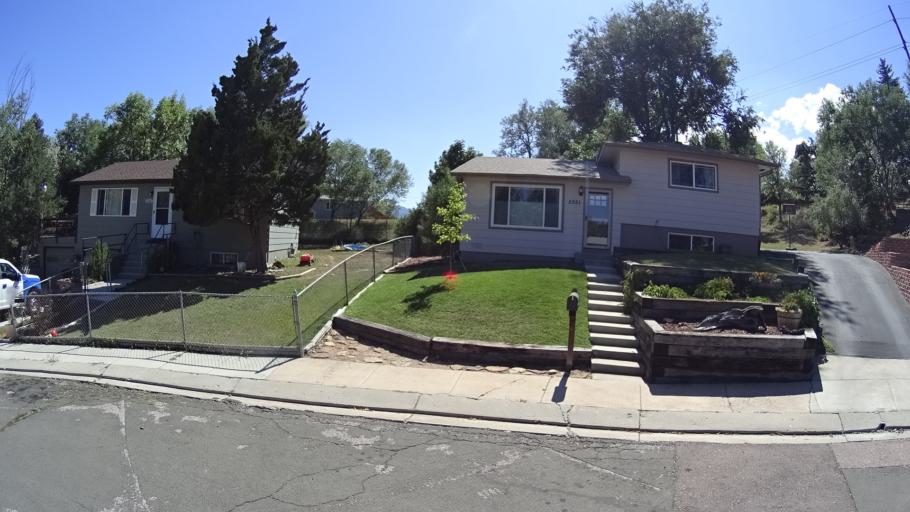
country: US
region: Colorado
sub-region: El Paso County
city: Colorado Springs
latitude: 38.8563
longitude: -104.8584
